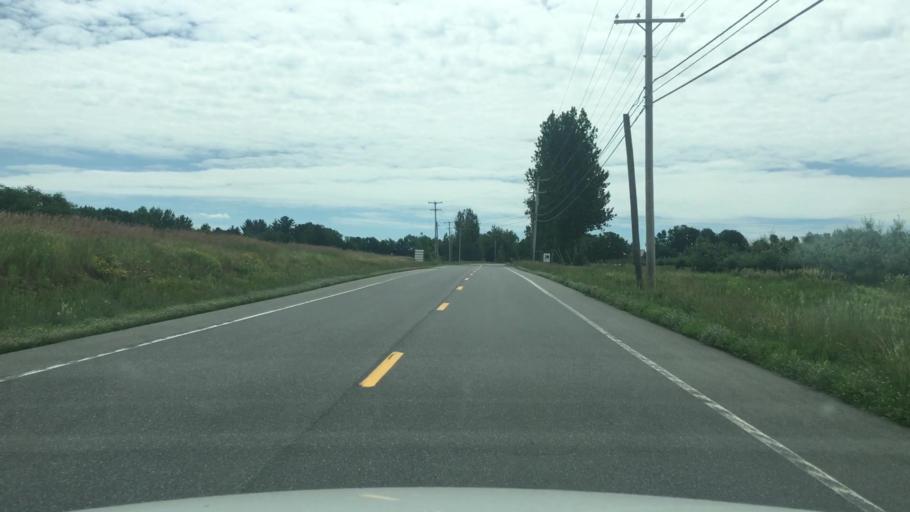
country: US
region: Maine
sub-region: Waldo County
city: Troy
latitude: 44.5639
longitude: -69.2742
